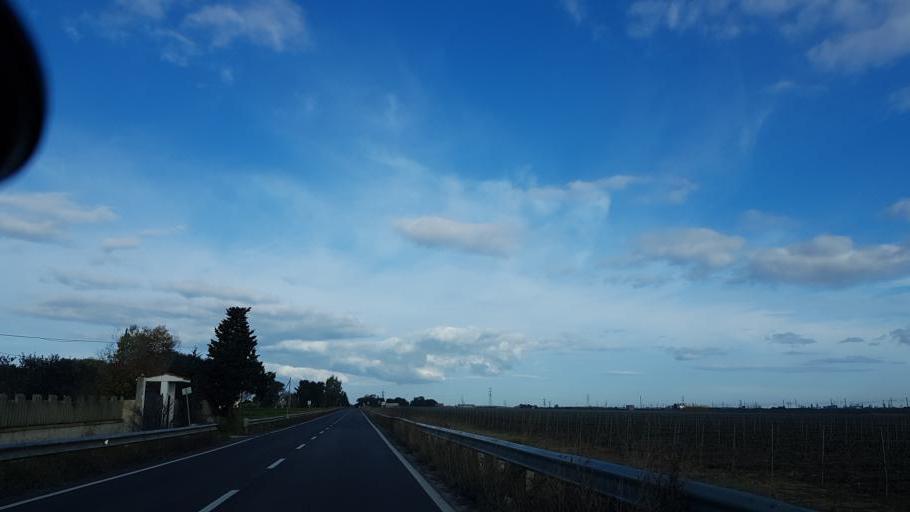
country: IT
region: Apulia
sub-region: Provincia di Brindisi
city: La Rosa
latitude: 40.5763
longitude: 17.9662
